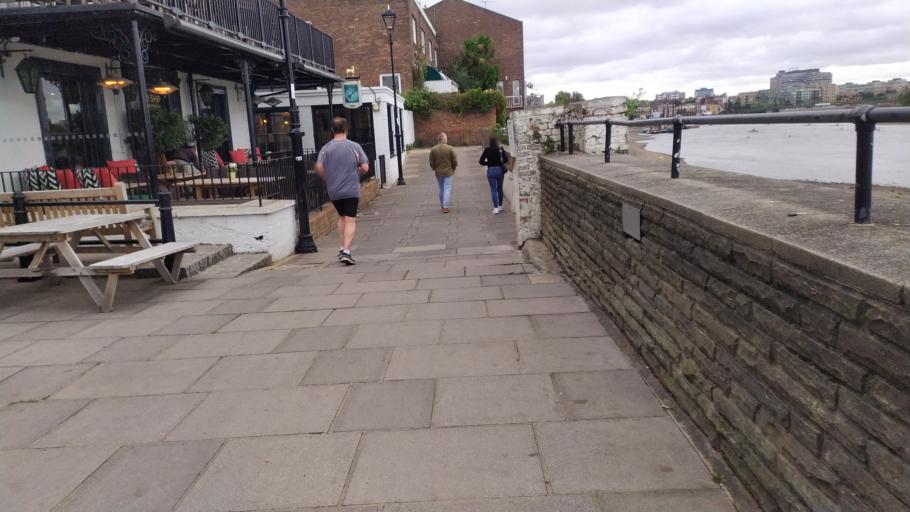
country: GB
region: England
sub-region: Greater London
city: Hammersmith
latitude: 51.4902
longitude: -0.2402
